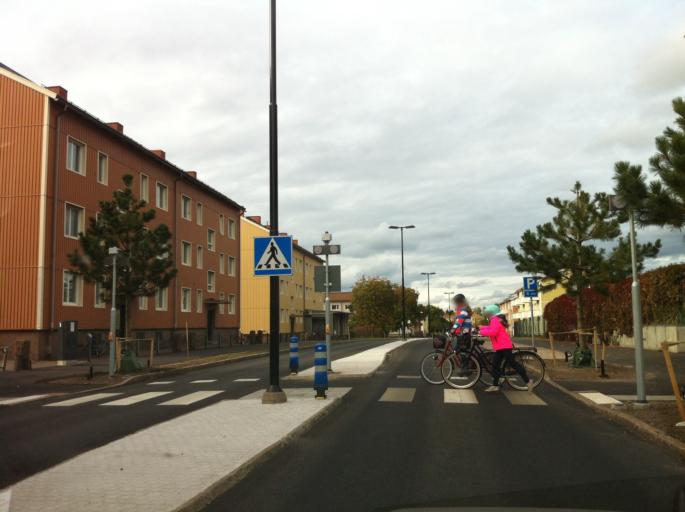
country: SE
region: OEstergoetland
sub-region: Motala Kommun
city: Motala
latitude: 58.5404
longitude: 15.0307
